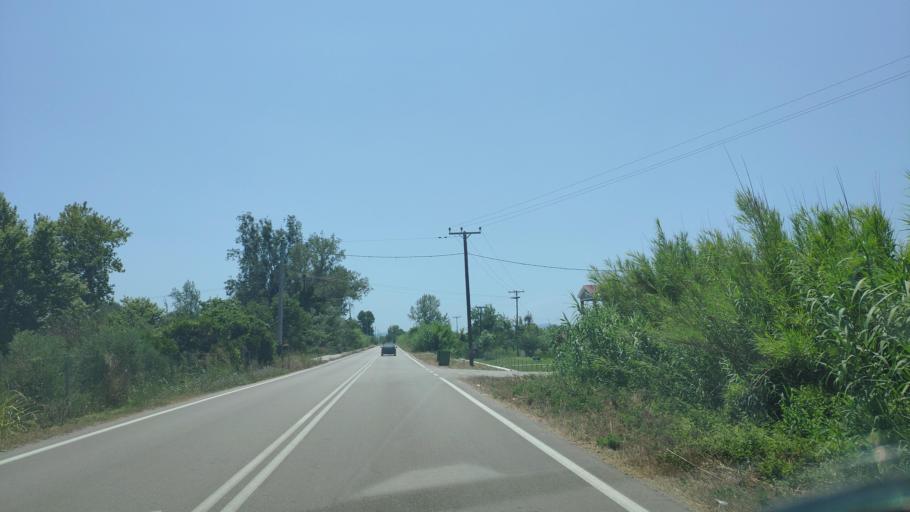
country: GR
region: Epirus
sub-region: Nomos Artas
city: Neochori
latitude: 39.0809
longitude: 21.0190
